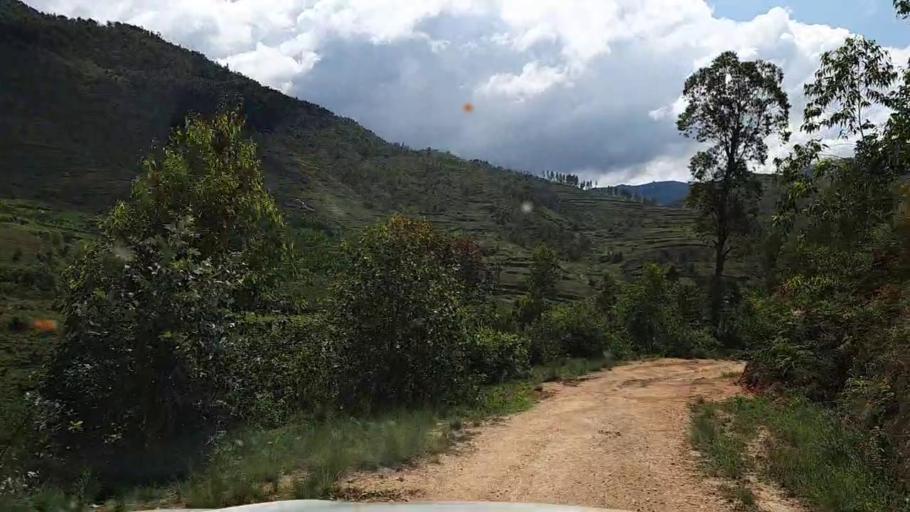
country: RW
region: Southern Province
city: Gikongoro
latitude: -2.3610
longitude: 29.5347
